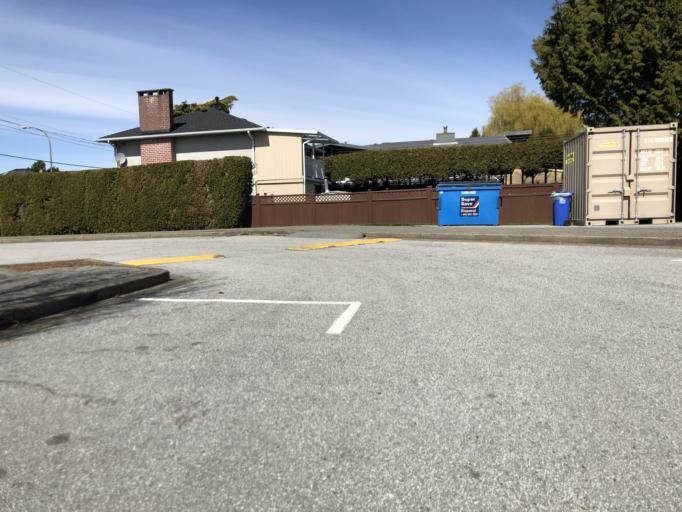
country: CA
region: British Columbia
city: Richmond
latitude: 49.1508
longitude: -123.1193
